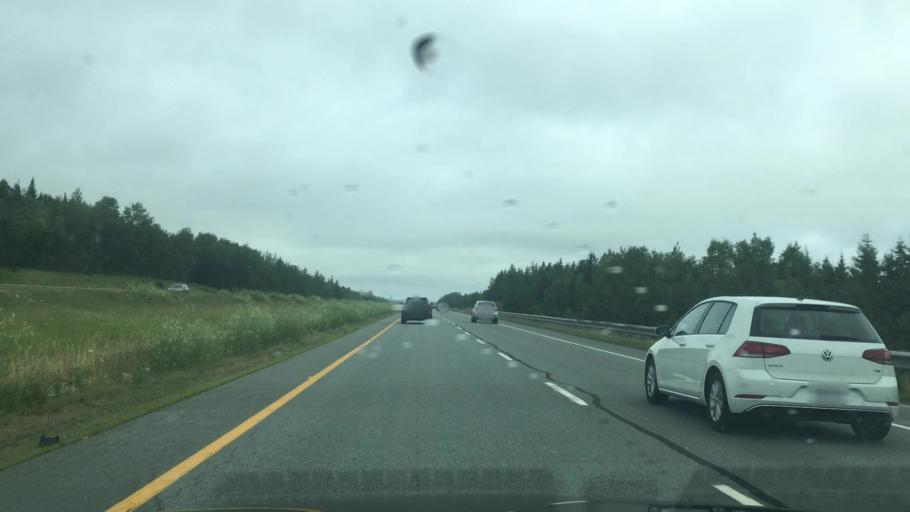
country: CA
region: Nova Scotia
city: Truro
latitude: 45.2780
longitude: -63.2954
